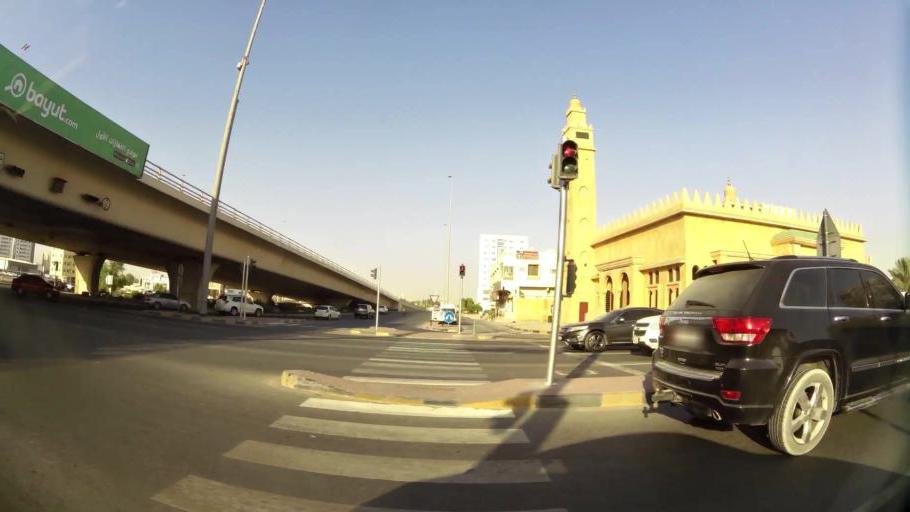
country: AE
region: Ajman
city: Ajman
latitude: 25.3982
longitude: 55.5046
